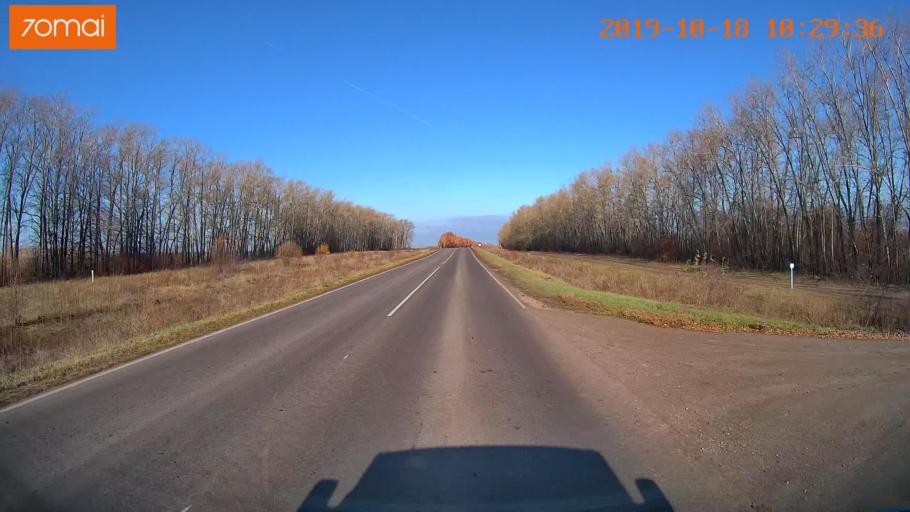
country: RU
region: Tula
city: Kurkino
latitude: 53.4535
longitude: 38.6543
